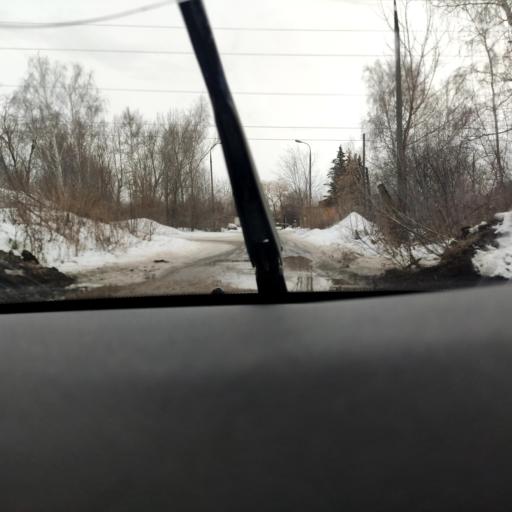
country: RU
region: Samara
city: Tol'yatti
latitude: 53.5515
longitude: 49.2960
